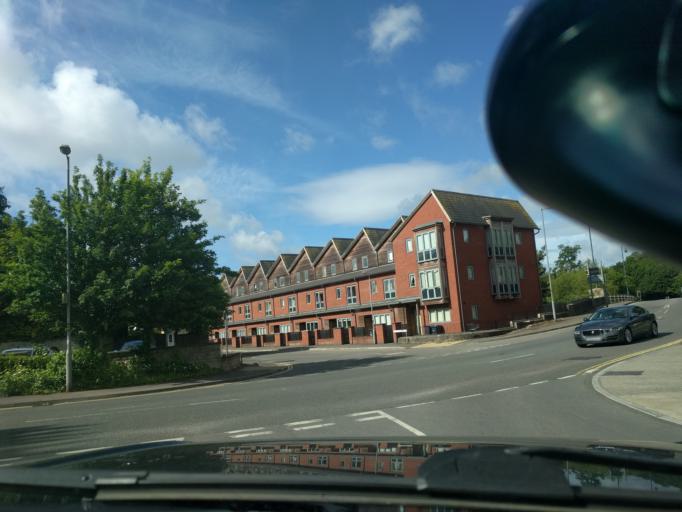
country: GB
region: England
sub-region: Wiltshire
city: Chippenham
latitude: 51.4577
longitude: -2.1166
